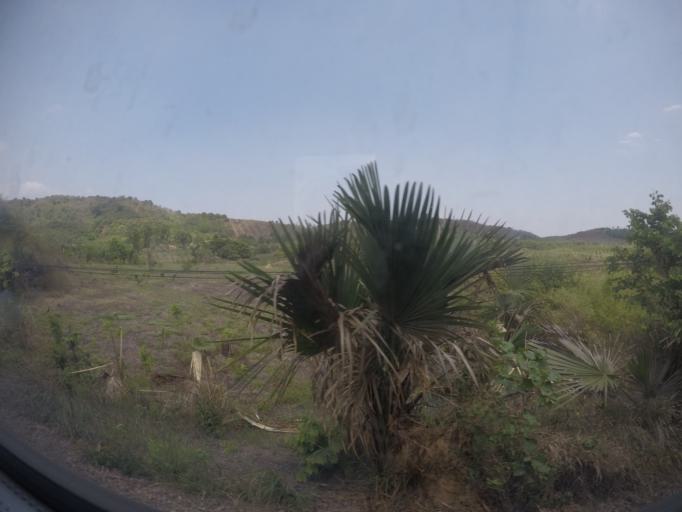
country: VN
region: Binh Thuan
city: Thuan Nam
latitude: 10.8731
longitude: 107.7087
